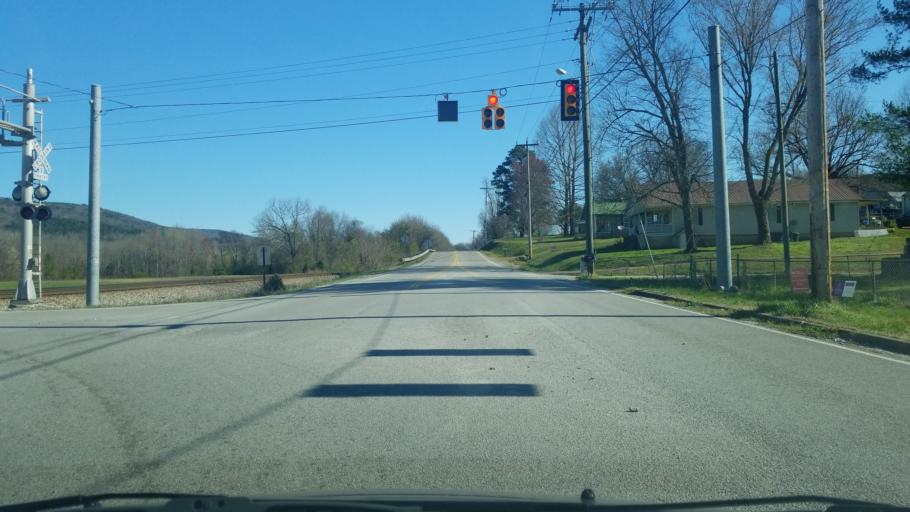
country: US
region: Tennessee
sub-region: Hamilton County
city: Soddy-Daisy
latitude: 35.2315
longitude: -85.1936
